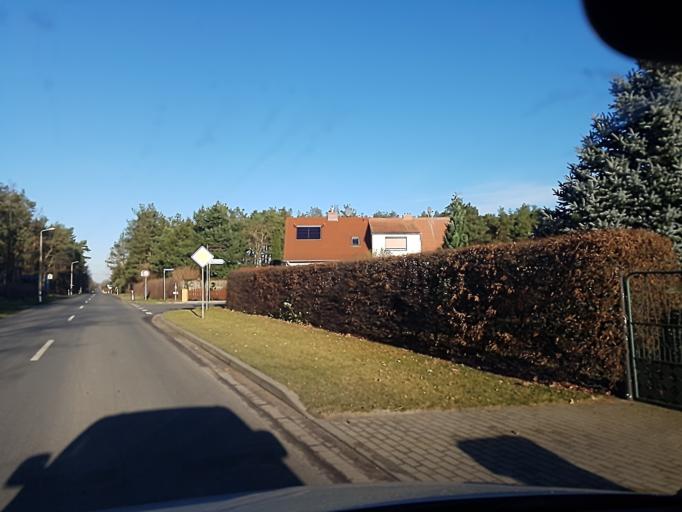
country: DE
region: Brandenburg
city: Finsterwalde
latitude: 51.6502
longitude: 13.7098
